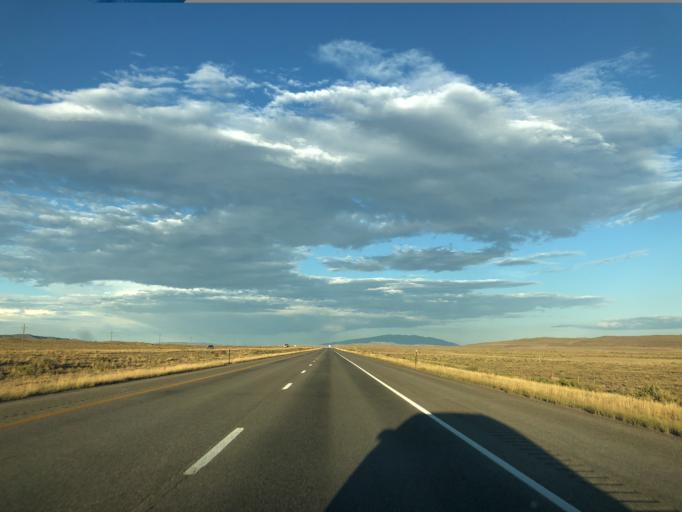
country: US
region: Wyoming
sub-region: Carbon County
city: Rawlins
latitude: 41.7672
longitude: -107.0366
